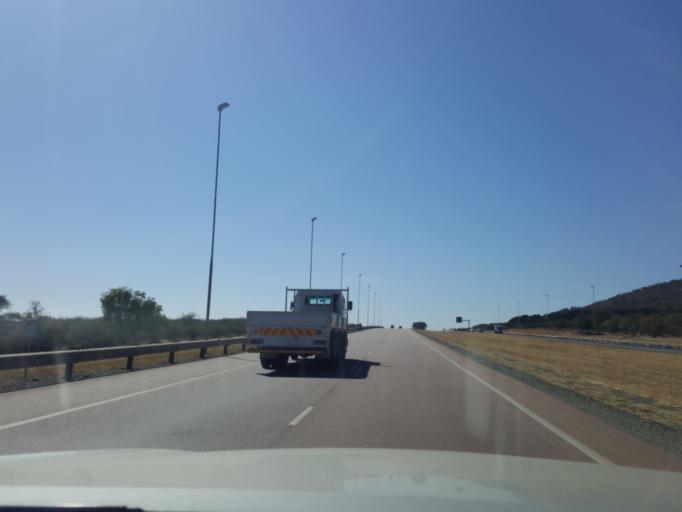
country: ZA
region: North-West
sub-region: Bojanala Platinum District Municipality
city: Brits
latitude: -25.7152
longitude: 27.6936
